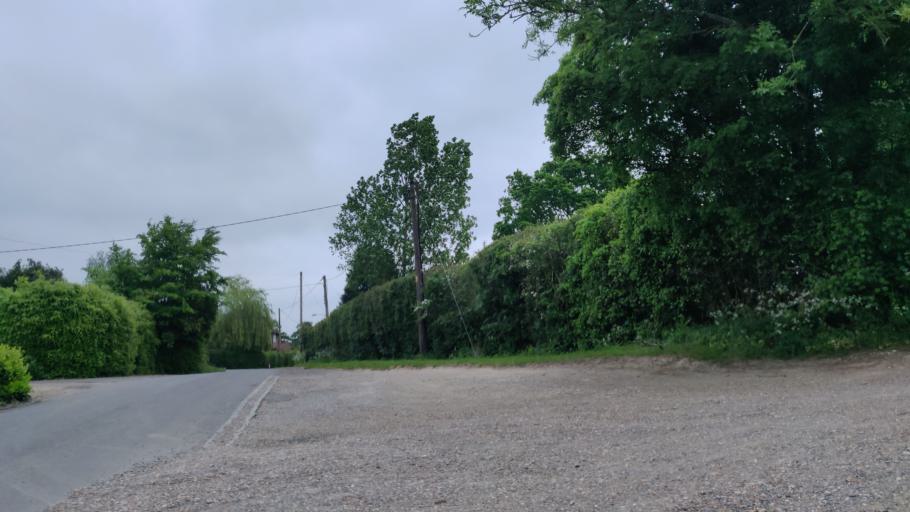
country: GB
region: England
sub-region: West Sussex
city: Southwater
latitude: 51.0114
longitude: -0.3326
